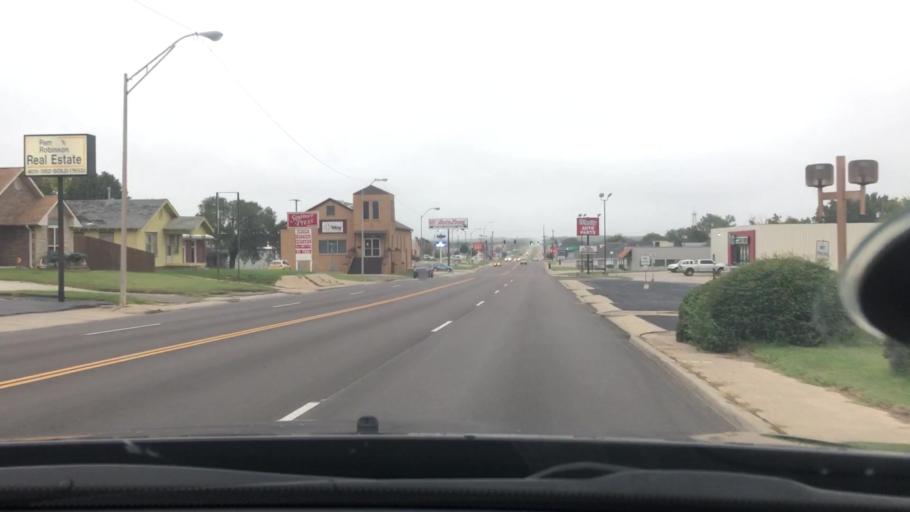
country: US
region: Oklahoma
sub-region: Seminole County
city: Seminole
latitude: 35.2291
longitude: -96.6710
